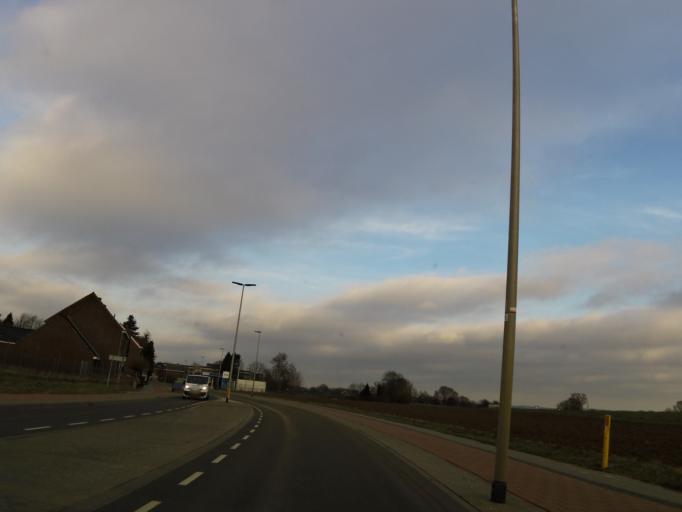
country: NL
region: Limburg
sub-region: Gemeente Nuth
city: Nuth
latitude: 50.9105
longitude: 5.8718
